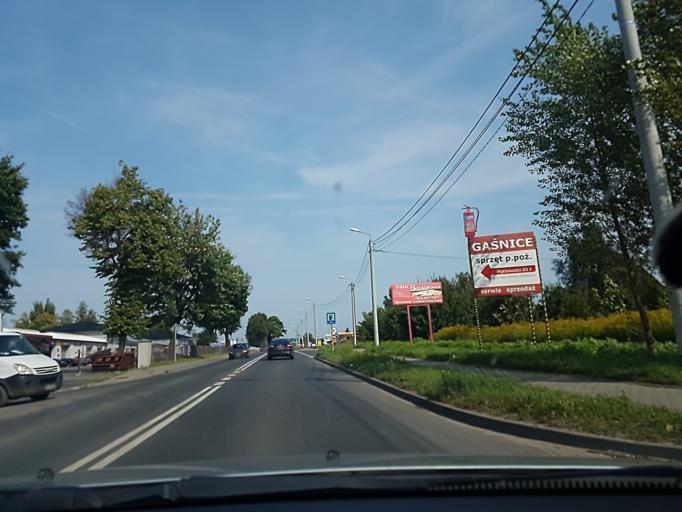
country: PL
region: Lodz Voivodeship
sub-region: Powiat zgierski
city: Zgierz
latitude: 51.8694
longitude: 19.4076
